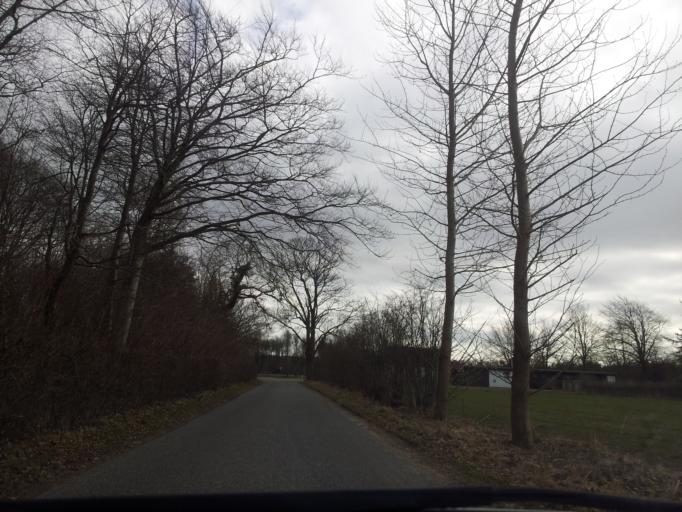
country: DK
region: South Denmark
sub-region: Vejen Kommune
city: Brorup
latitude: 55.4470
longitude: 9.0463
